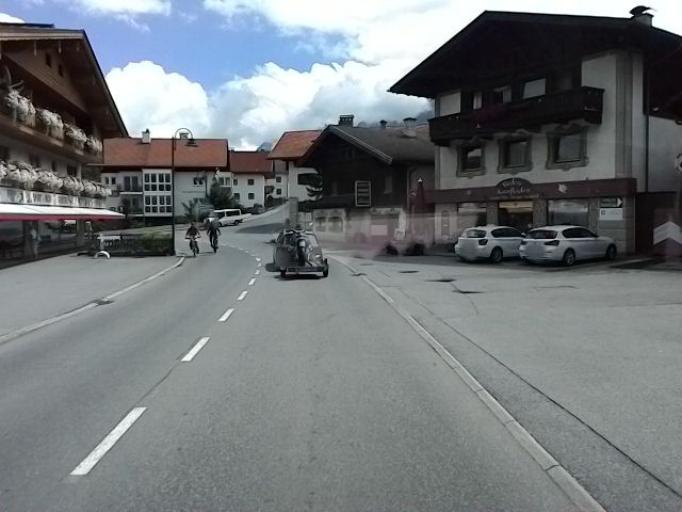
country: AT
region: Tyrol
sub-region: Politischer Bezirk Reutte
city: Lermoos
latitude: 47.4011
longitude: 10.8834
